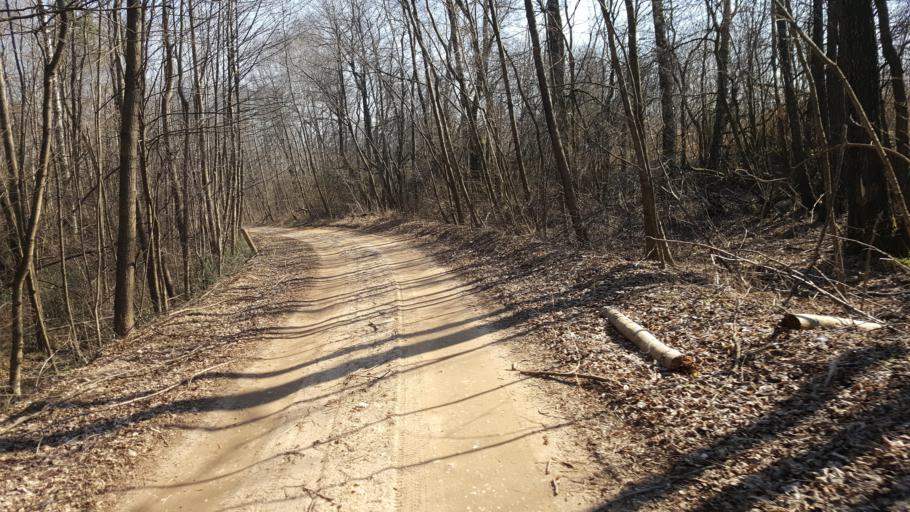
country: BY
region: Brest
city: Kamyanyets
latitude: 52.3666
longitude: 23.7523
